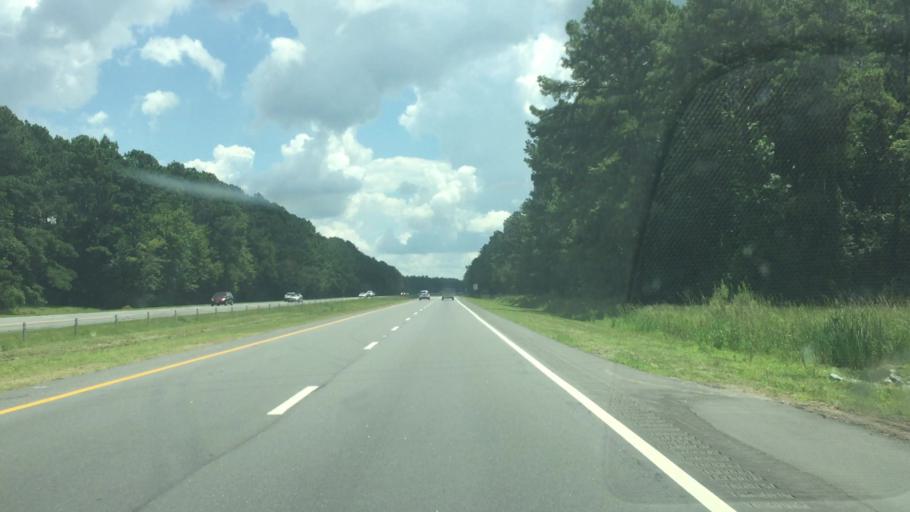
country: US
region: North Carolina
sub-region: Columbus County
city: Chadbourn
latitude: 34.3858
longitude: -78.8695
